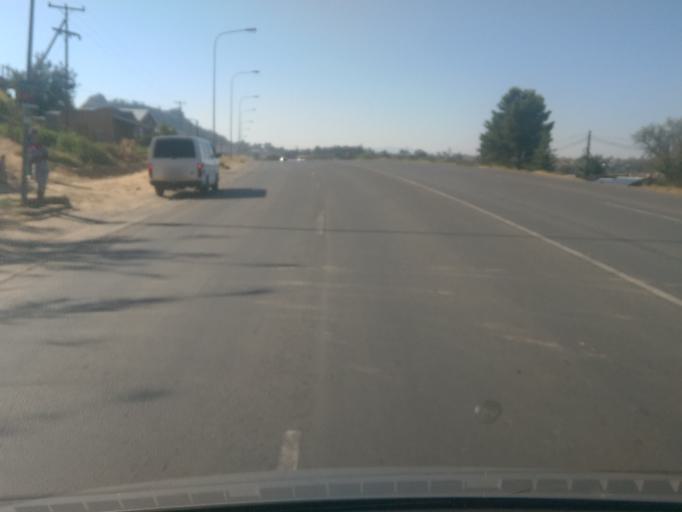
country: LS
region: Maseru
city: Maseru
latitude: -29.3529
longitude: 27.5217
